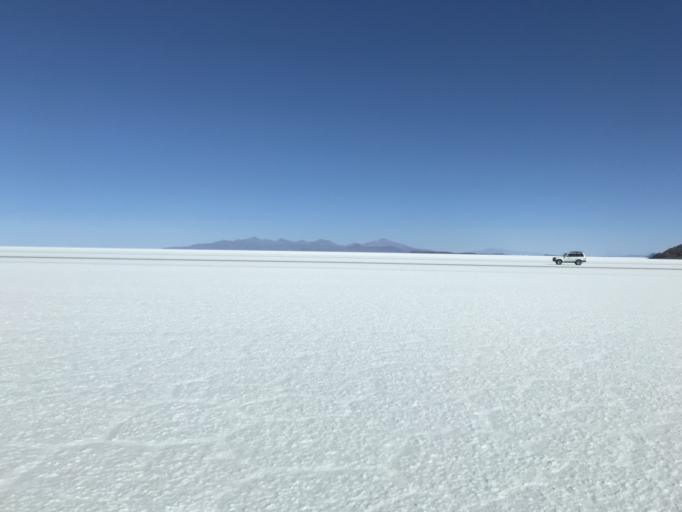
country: BO
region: Potosi
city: Colchani
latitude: -20.2385
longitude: -67.6177
